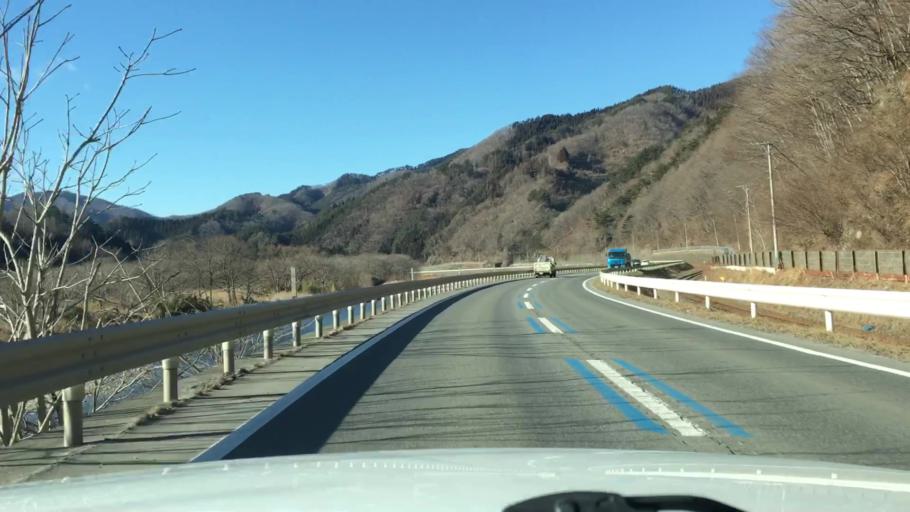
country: JP
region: Iwate
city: Miyako
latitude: 39.6303
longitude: 141.8547
